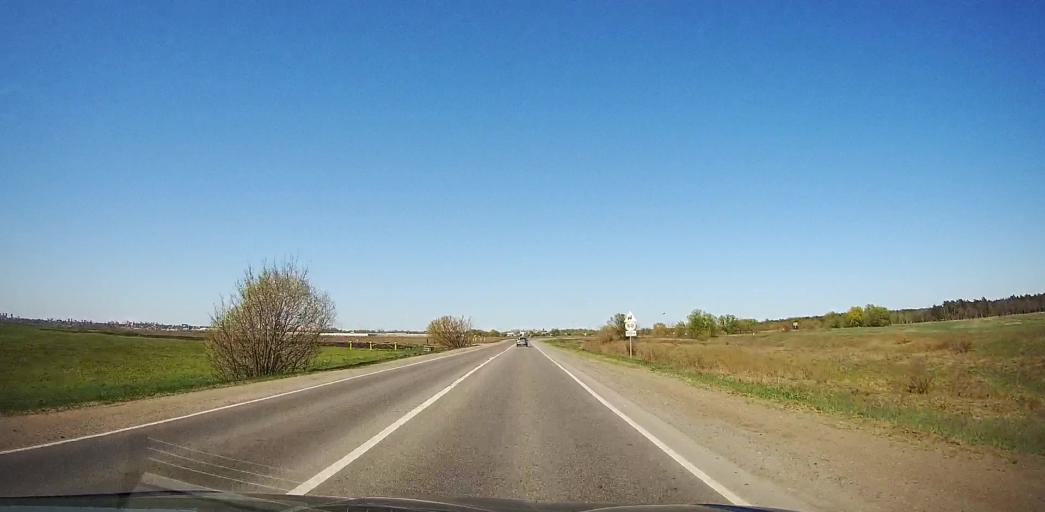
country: RU
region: Moskovskaya
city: Ramenskoye
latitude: 55.5248
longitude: 38.2772
